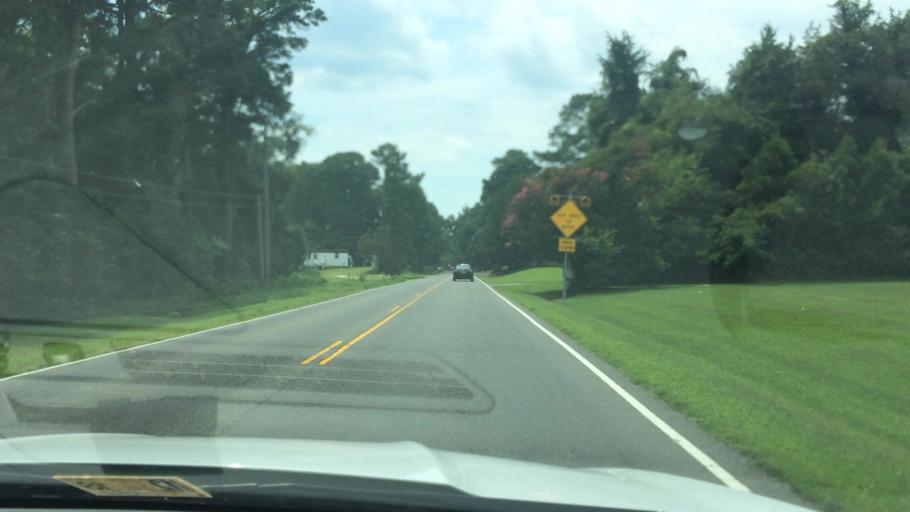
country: US
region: Virginia
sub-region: Lancaster County
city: Kilmarnock
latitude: 37.6425
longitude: -76.4014
